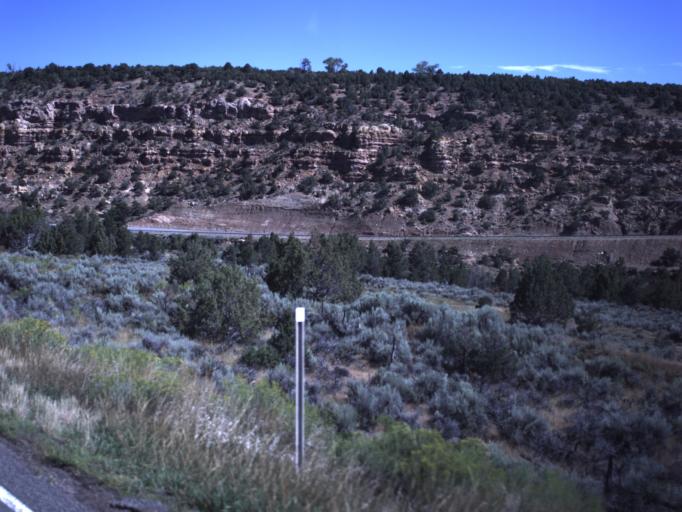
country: US
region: Utah
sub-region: Duchesne County
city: Duchesne
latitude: 40.3562
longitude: -110.3960
